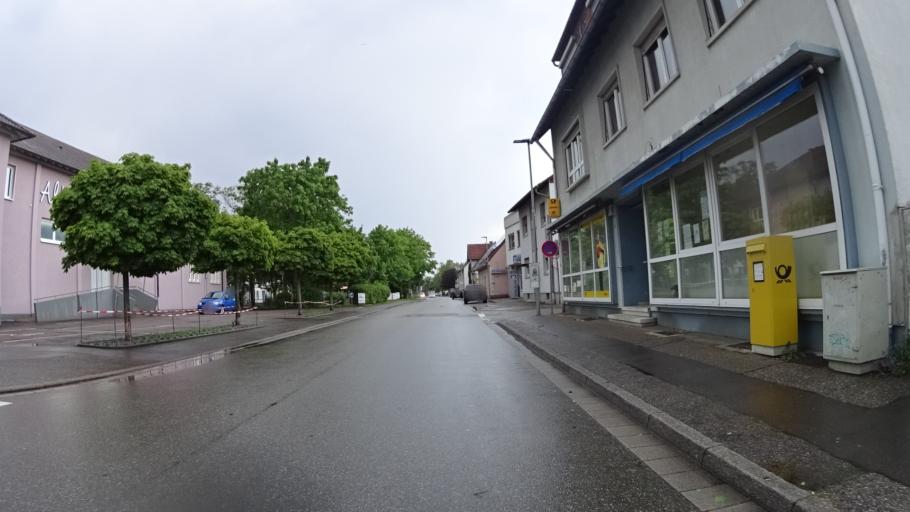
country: DE
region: Baden-Wuerttemberg
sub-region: Karlsruhe Region
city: Durmersheim
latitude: 48.9343
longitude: 8.2727
